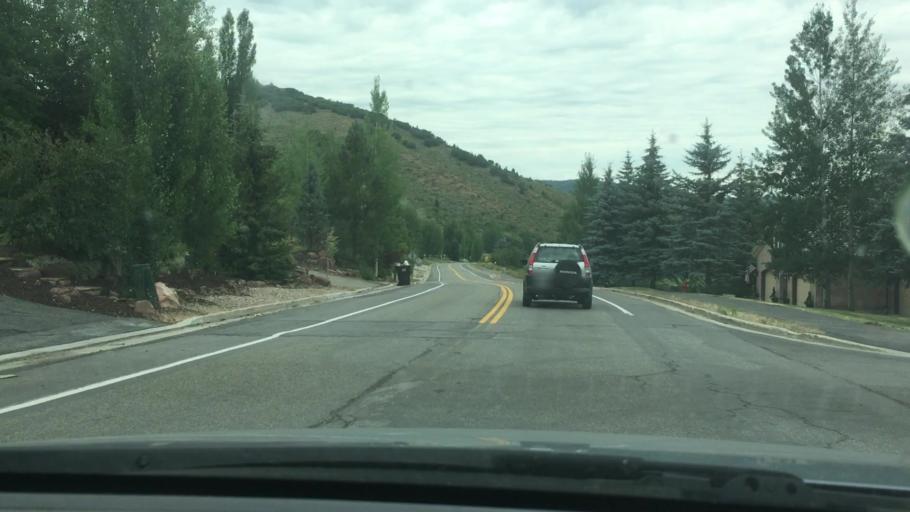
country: US
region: Utah
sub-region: Summit County
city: Summit Park
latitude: 40.7630
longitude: -111.5795
